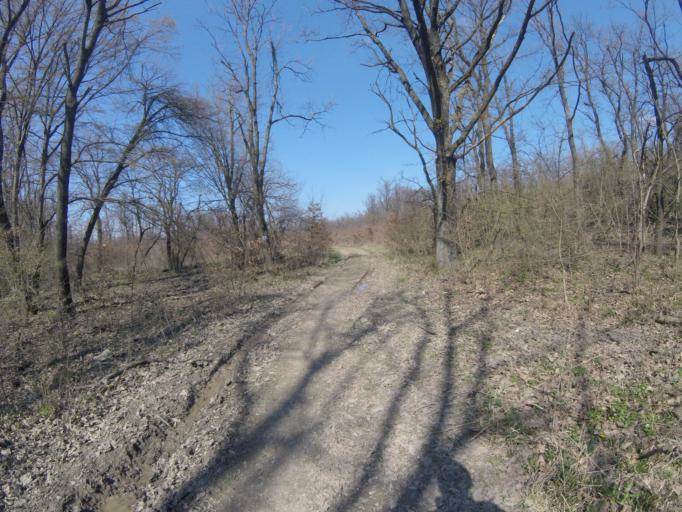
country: HU
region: Pest
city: Budakeszi
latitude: 47.5423
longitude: 18.8901
